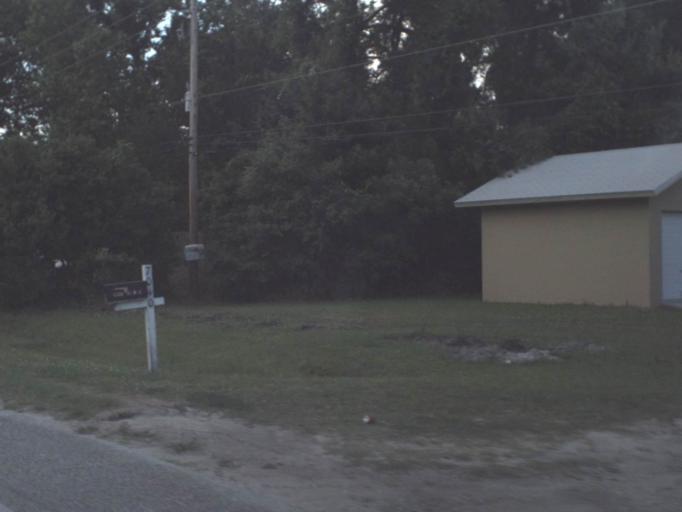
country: US
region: Florida
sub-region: Saint Johns County
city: Villano Beach
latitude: 30.0024
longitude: -81.3829
